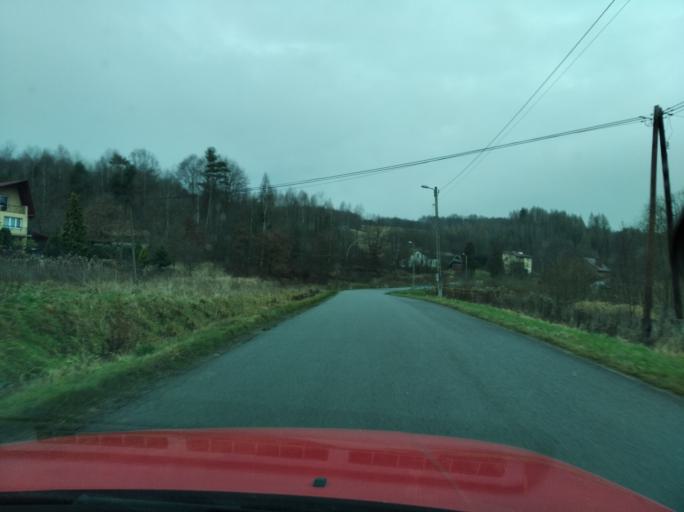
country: PL
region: Subcarpathian Voivodeship
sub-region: Powiat przemyski
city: Nienadowa
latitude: 49.8520
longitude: 22.4242
